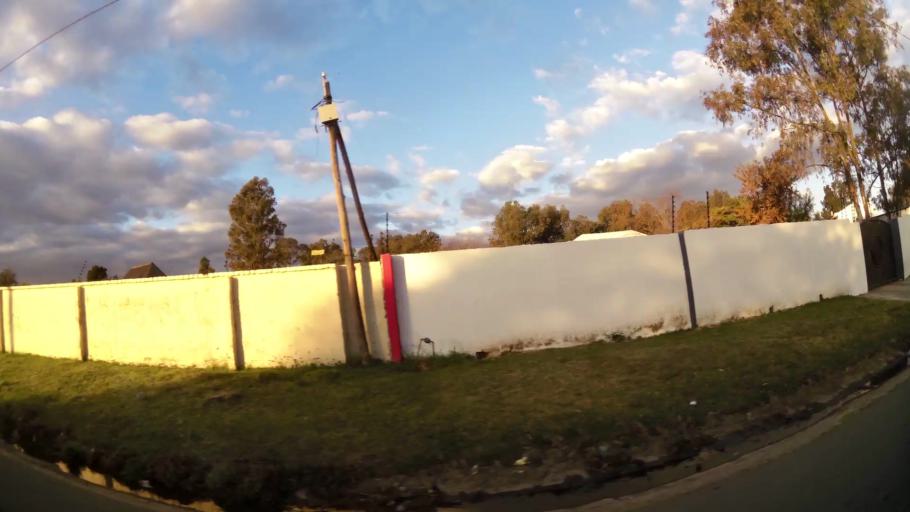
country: ZA
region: Gauteng
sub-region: City of Johannesburg Metropolitan Municipality
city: Midrand
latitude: -26.0037
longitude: 28.1522
